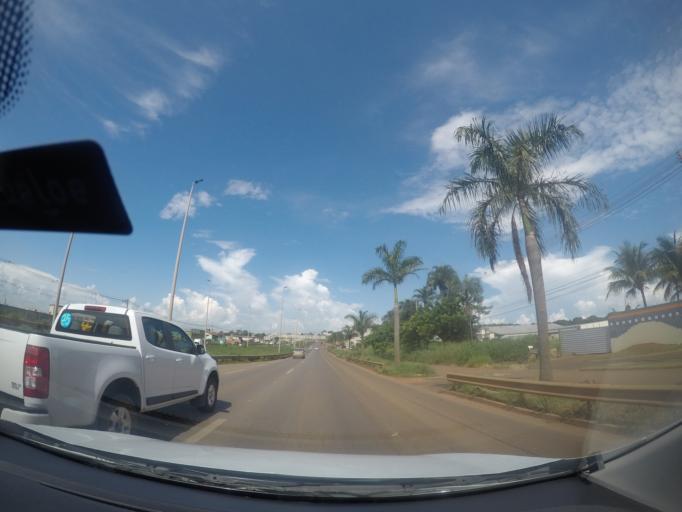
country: BR
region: Goias
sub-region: Goiania
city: Goiania
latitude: -16.6594
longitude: -49.3604
